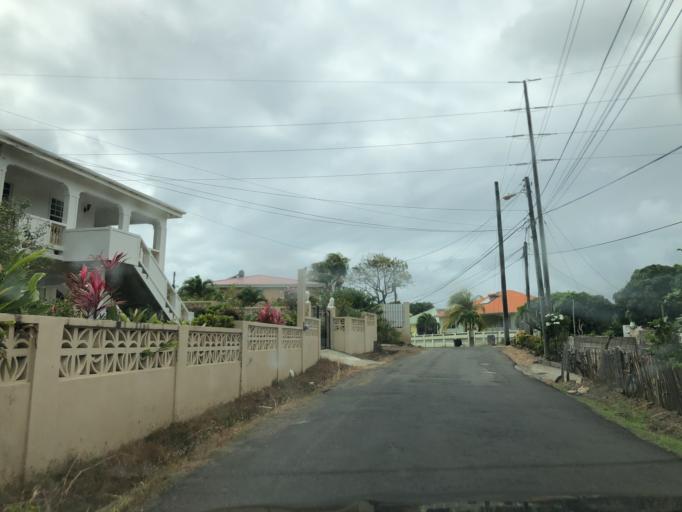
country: LC
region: Gros-Islet
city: Gros Islet
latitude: 14.0673
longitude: -60.9461
